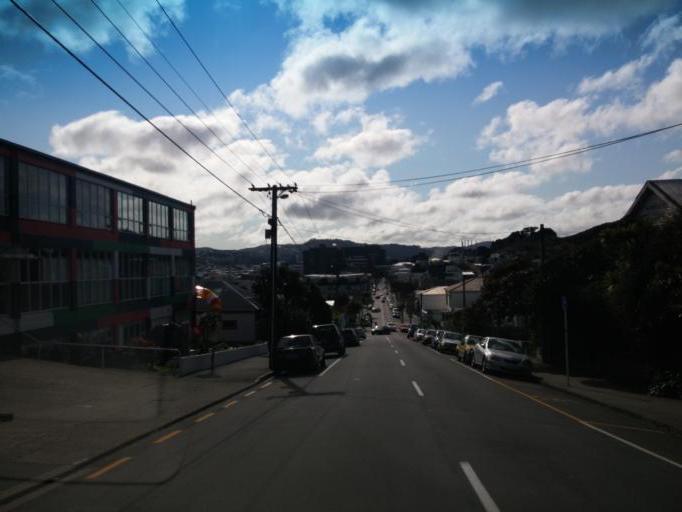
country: NZ
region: Wellington
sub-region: Wellington City
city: Wellington
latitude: -41.3160
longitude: 174.7832
